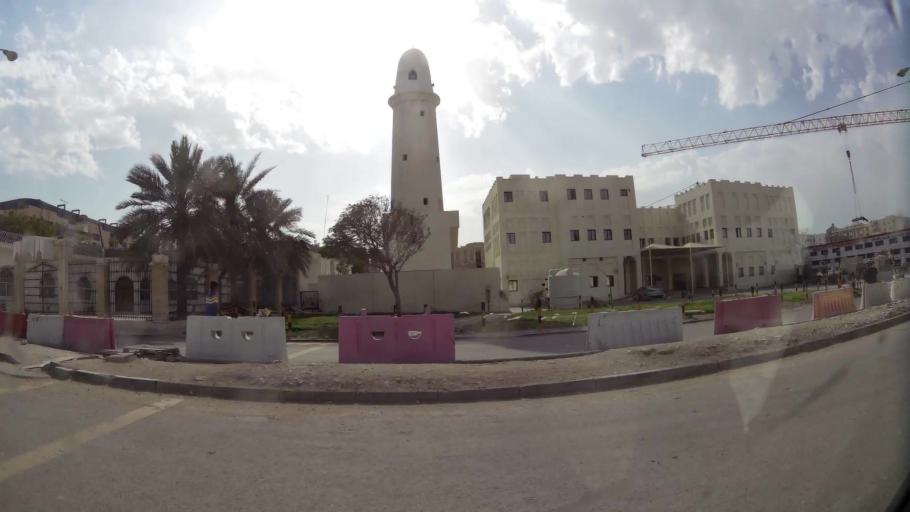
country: QA
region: Baladiyat ad Dawhah
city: Doha
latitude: 25.2801
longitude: 51.5158
